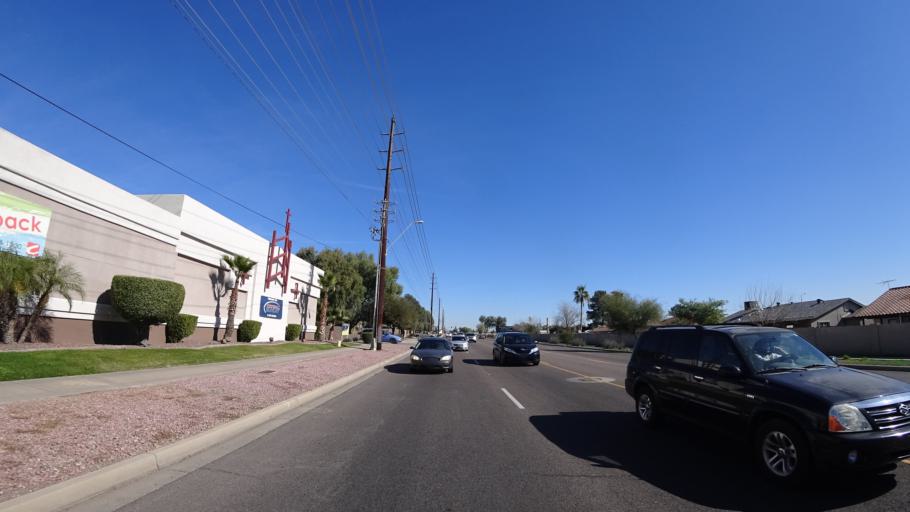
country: US
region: Arizona
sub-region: Maricopa County
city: Glendale
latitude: 33.5090
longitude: -112.2238
